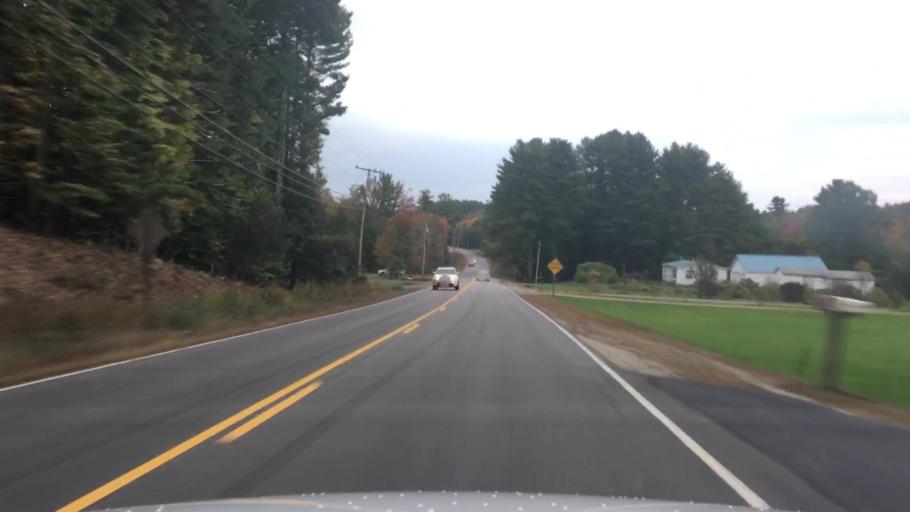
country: US
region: Maine
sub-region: York County
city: Hollis Center
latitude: 43.6076
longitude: -70.5788
